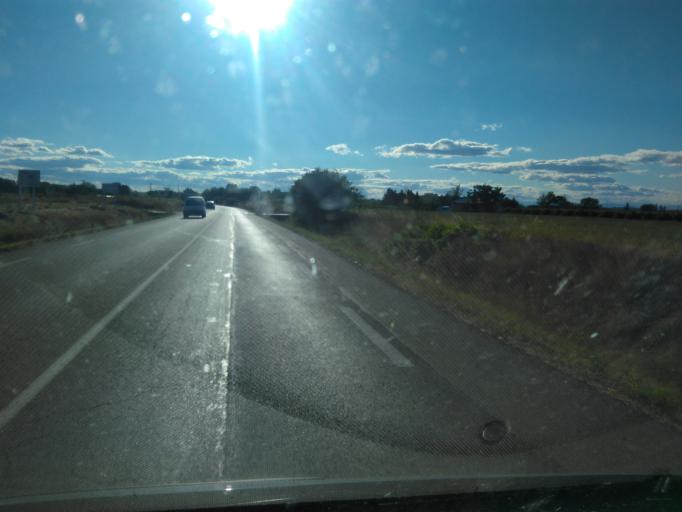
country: FR
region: Languedoc-Roussillon
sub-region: Departement du Gard
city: Le Cailar
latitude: 43.6871
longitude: 4.2297
